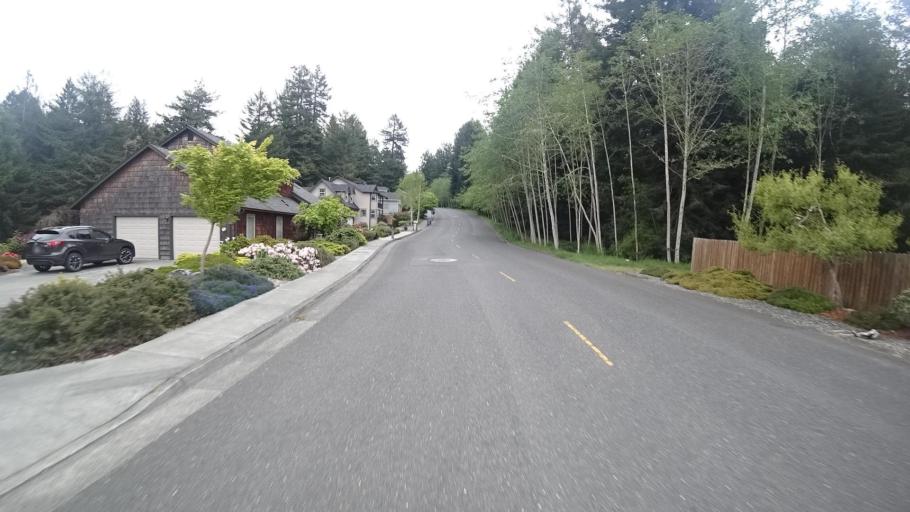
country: US
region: California
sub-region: Humboldt County
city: Arcata
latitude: 40.8858
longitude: -124.0714
